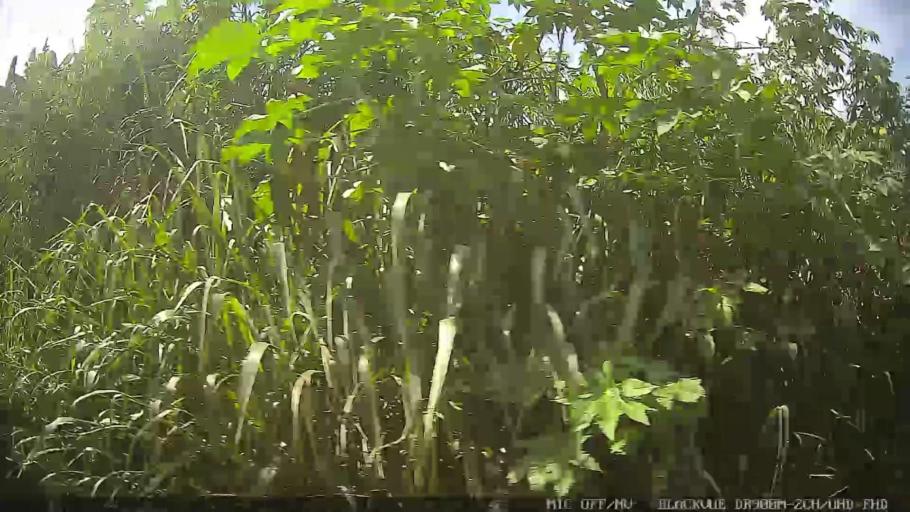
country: BR
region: Sao Paulo
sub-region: Suzano
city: Suzano
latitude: -23.4917
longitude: -46.2858
